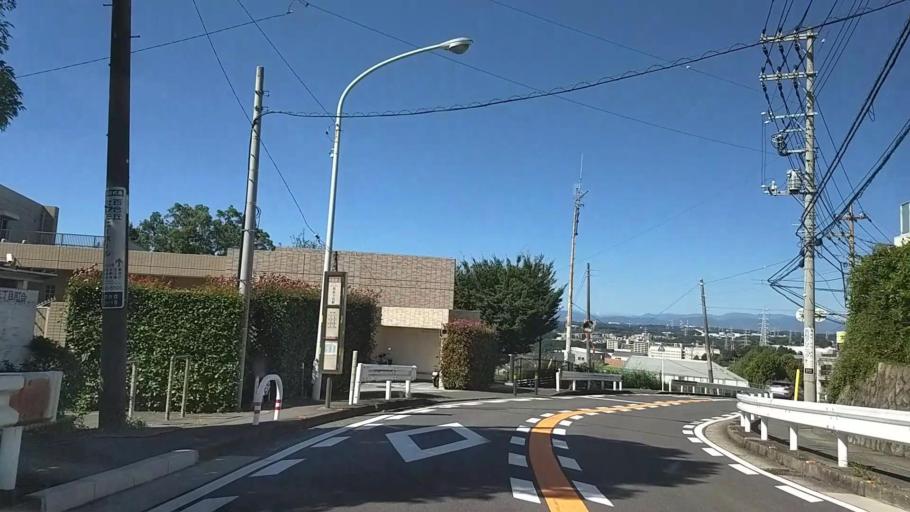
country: JP
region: Tokyo
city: Chofugaoka
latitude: 35.5997
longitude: 139.5209
